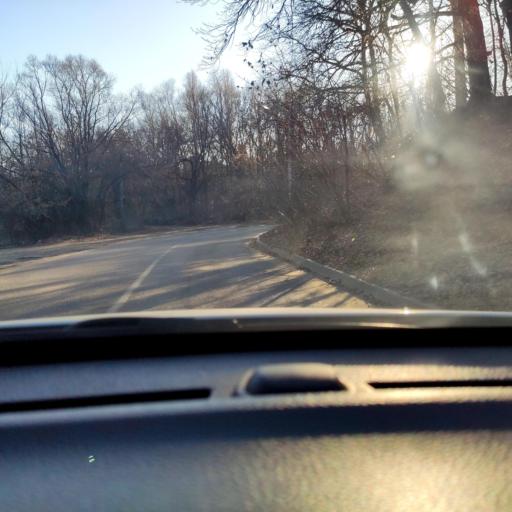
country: RU
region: Voronezj
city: Voronezh
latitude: 51.7230
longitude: 39.2367
